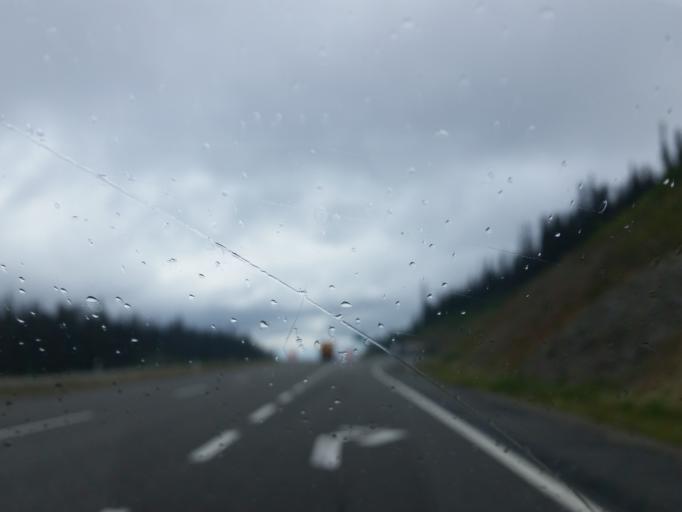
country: CA
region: British Columbia
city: Peachland
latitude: 49.9063
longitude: -120.0108
